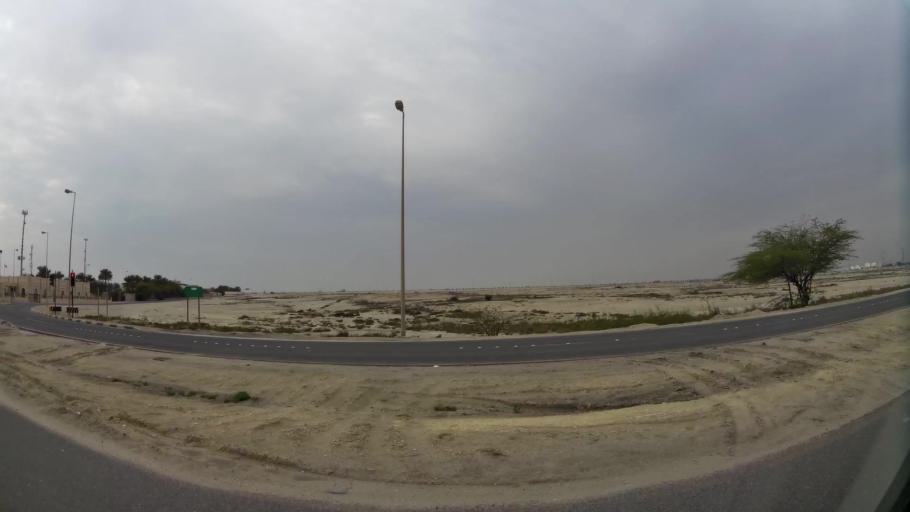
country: BH
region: Northern
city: Ar Rifa'
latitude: 26.0624
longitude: 50.6170
